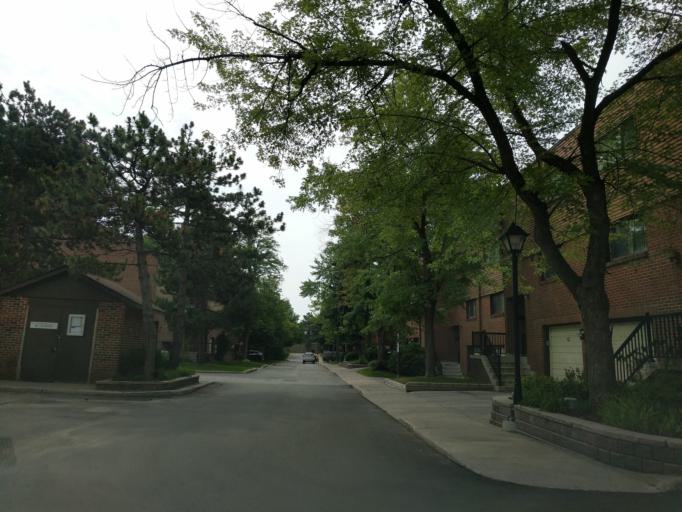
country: CA
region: Ontario
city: Willowdale
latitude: 43.8113
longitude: -79.3568
